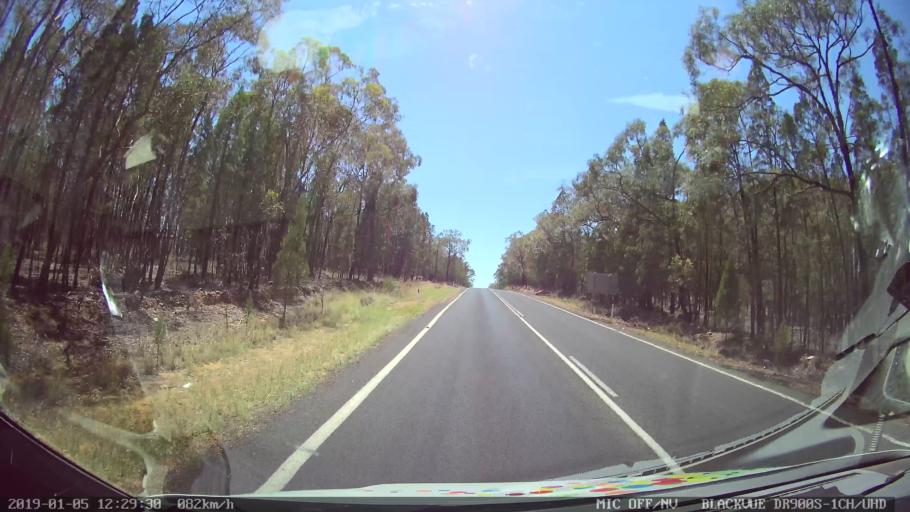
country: AU
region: New South Wales
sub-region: Warrumbungle Shire
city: Coonabarabran
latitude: -31.2328
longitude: 149.3380
